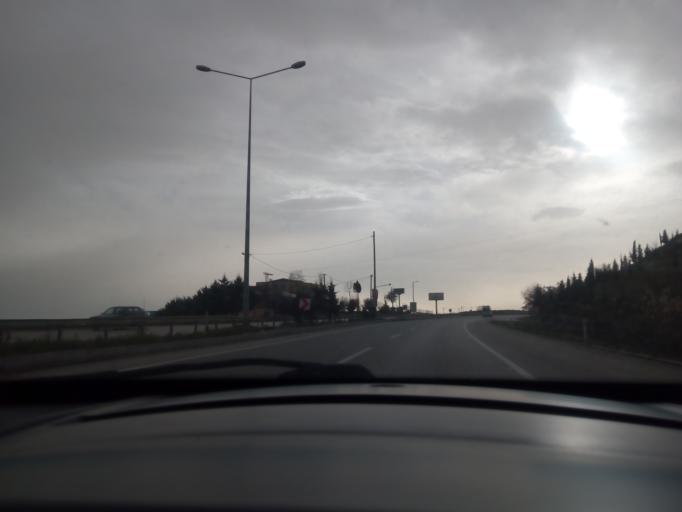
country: TR
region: Bursa
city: Tatkavakli
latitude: 40.0497
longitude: 28.3719
